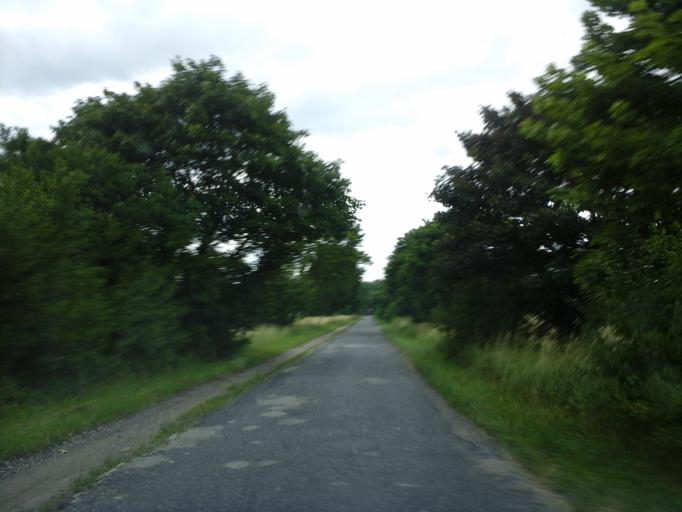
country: PL
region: West Pomeranian Voivodeship
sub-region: Powiat choszczenski
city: Bierzwnik
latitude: 52.9998
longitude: 15.6355
